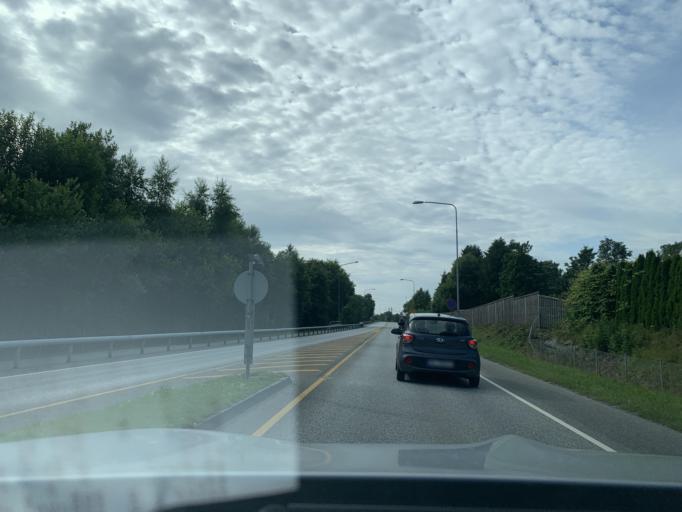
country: NO
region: Rogaland
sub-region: Stavanger
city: Stavanger
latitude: 58.9181
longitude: 5.7160
